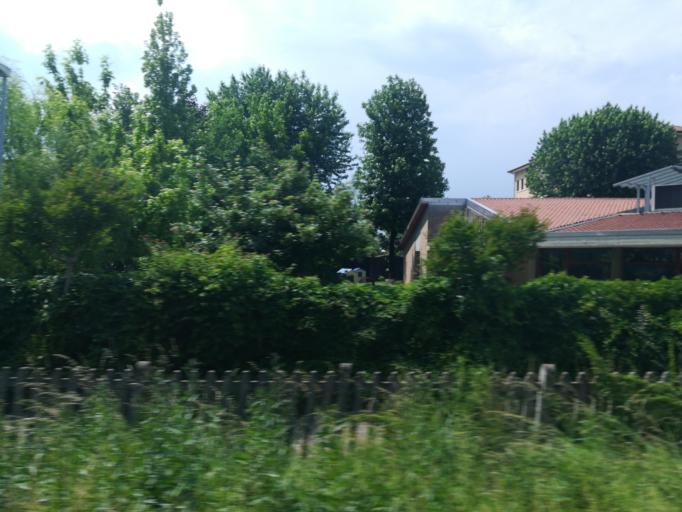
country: IT
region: Veneto
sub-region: Provincia di Vicenza
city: Monticello Conte Otto
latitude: 45.6015
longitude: 11.5701
